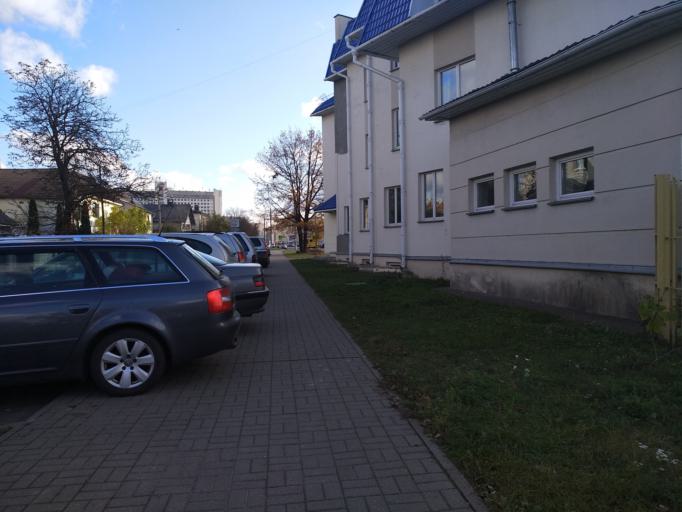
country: BY
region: Minsk
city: Minsk
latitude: 53.9397
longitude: 27.5743
